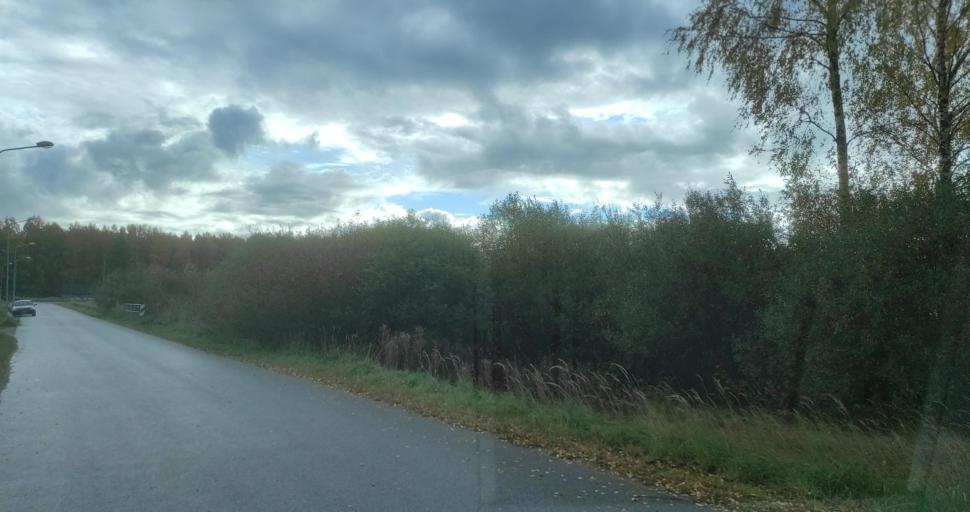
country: LV
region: Skrunda
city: Skrunda
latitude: 56.6855
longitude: 22.0042
